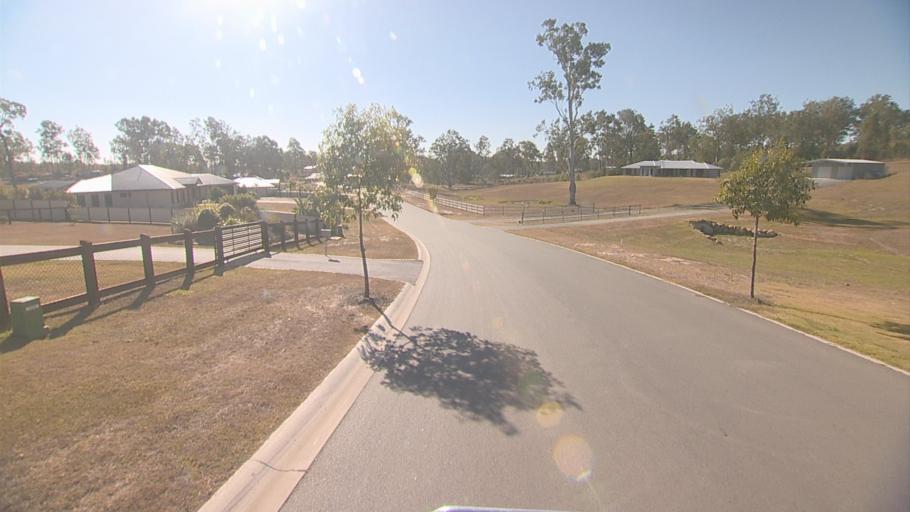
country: AU
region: Queensland
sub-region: Logan
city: Cedar Vale
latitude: -27.8719
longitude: 153.0564
